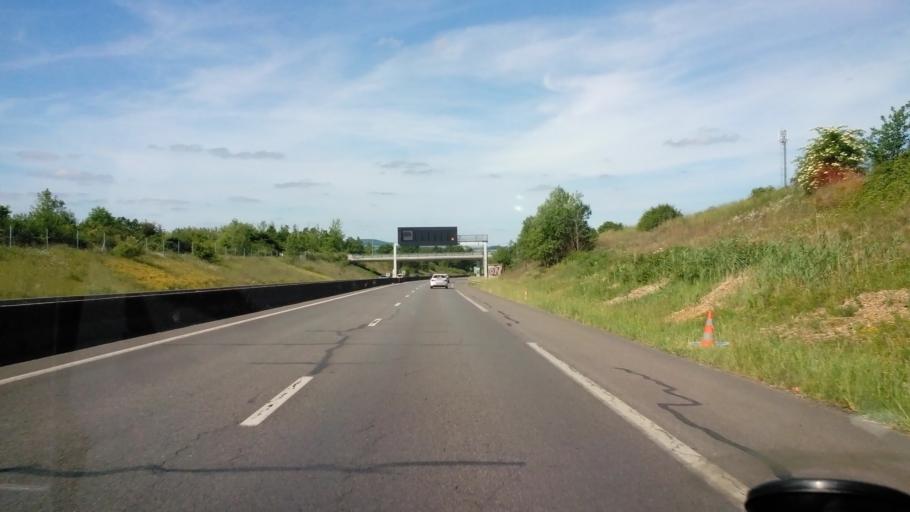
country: FR
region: Lorraine
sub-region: Departement de la Moselle
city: Marly
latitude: 49.0524
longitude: 6.1704
